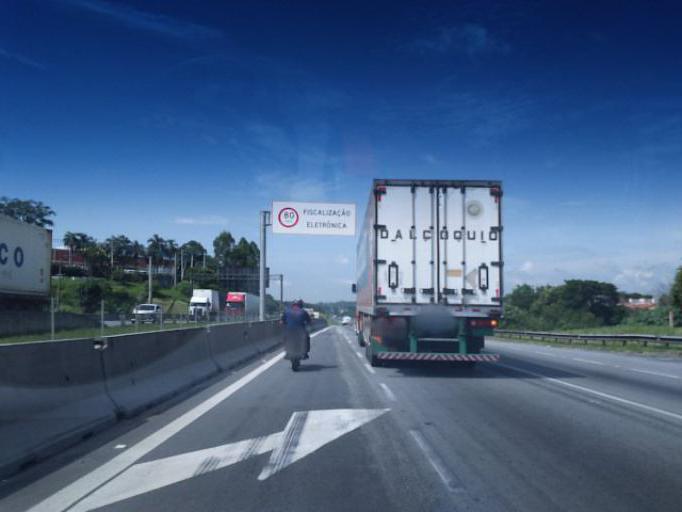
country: BR
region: Sao Paulo
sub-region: Embu
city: Embu
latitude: -23.6470
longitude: -46.8425
